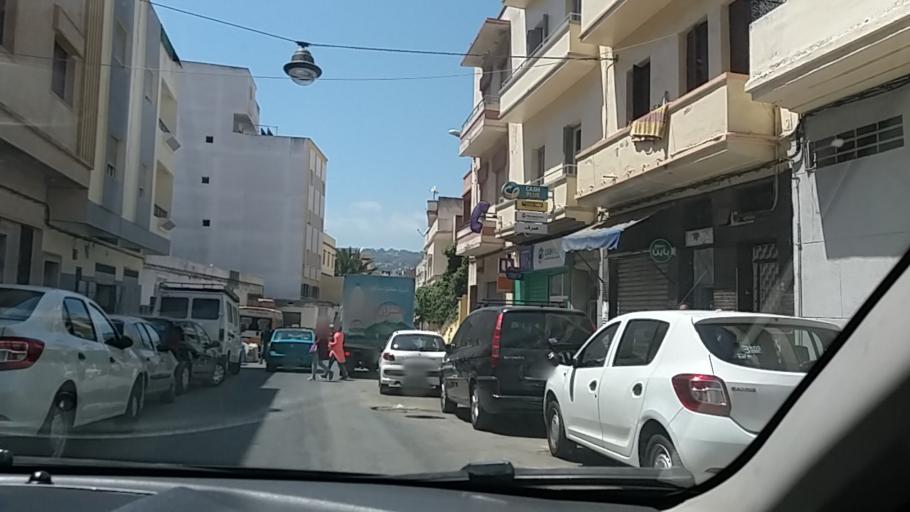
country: MA
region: Tanger-Tetouan
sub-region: Tanger-Assilah
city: Tangier
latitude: 35.7860
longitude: -5.8253
